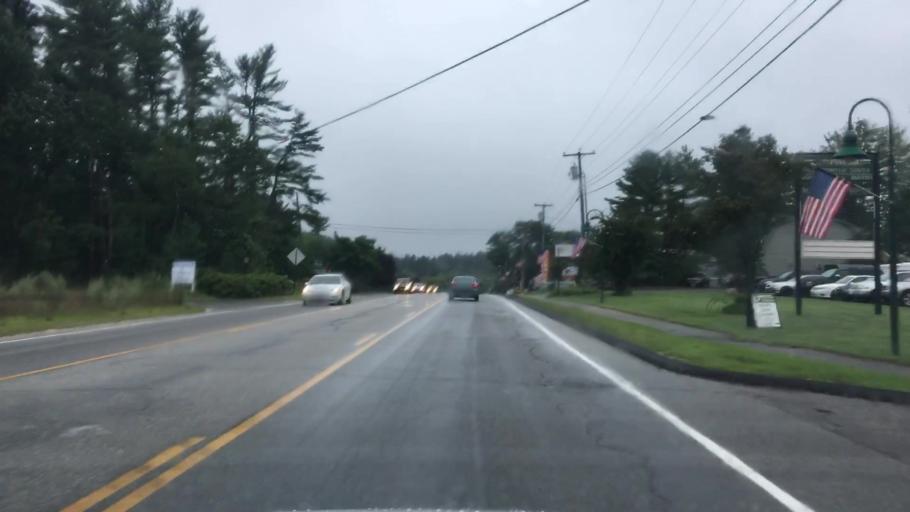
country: US
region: Maine
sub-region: Cumberland County
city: Raymond
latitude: 43.8832
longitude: -70.4653
